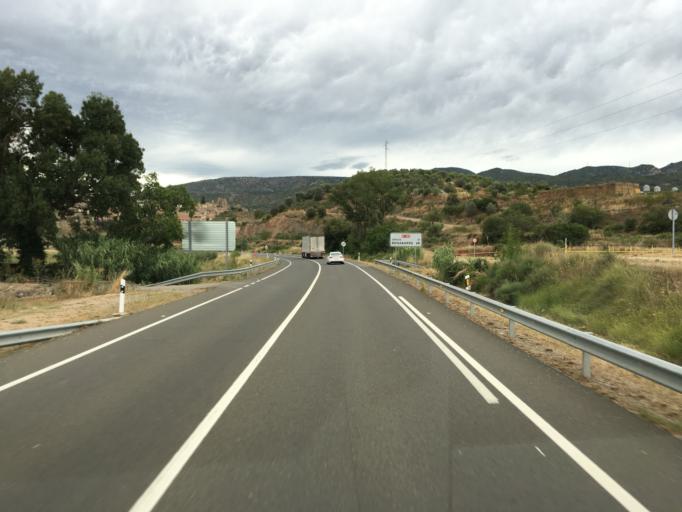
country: ES
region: Aragon
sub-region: Provincia de Huesca
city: Estada
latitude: 42.0662
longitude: 0.2246
